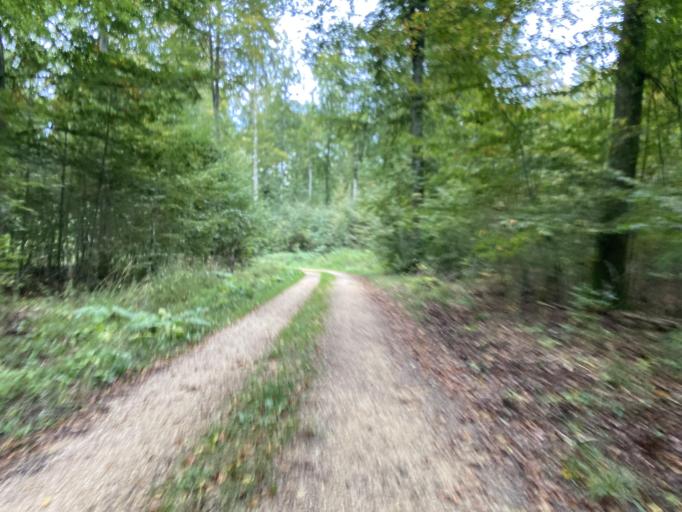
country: DE
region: Baden-Wuerttemberg
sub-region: Tuebingen Region
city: Sigmaringen
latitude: 48.1090
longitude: 9.2193
